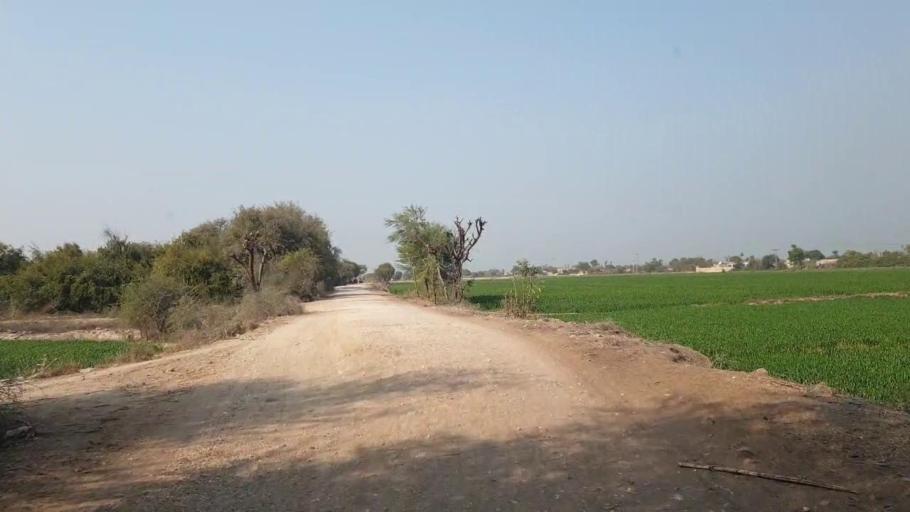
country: PK
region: Sindh
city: Hala
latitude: 25.8737
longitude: 68.4618
